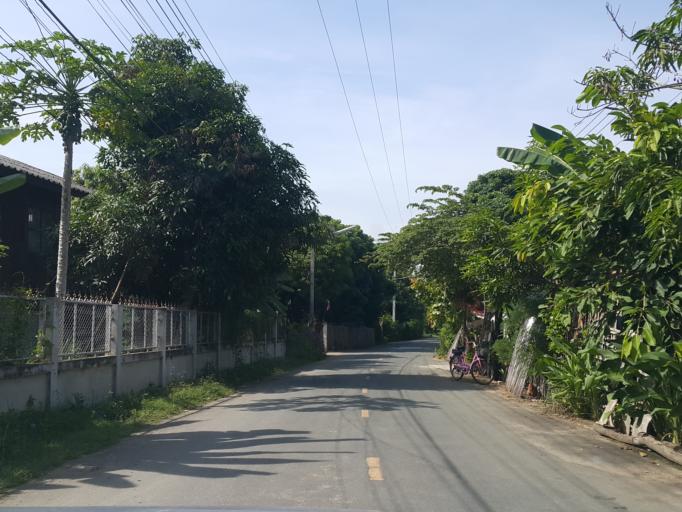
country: TH
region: Chiang Mai
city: San Kamphaeng
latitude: 18.7185
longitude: 99.0951
